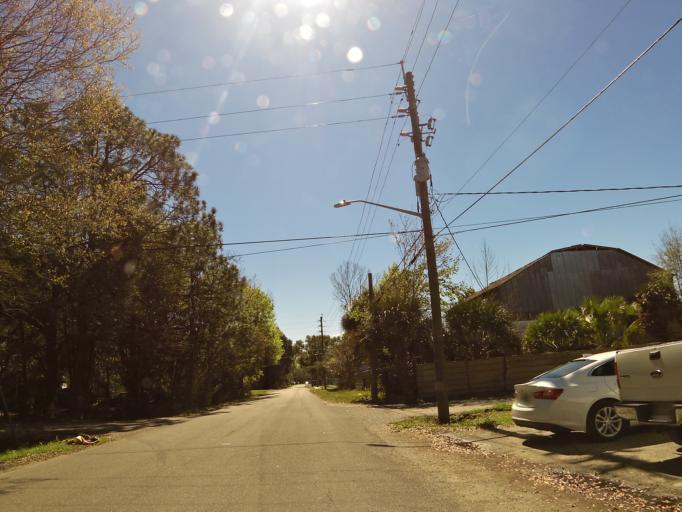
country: US
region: Florida
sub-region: Duval County
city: Jacksonville
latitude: 30.3256
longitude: -81.7174
